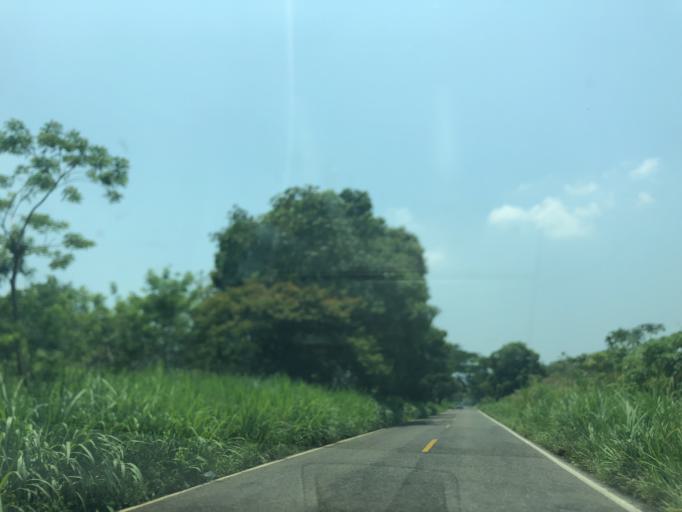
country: MX
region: Tabasco
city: Teapa
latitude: 17.5555
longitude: -93.0015
